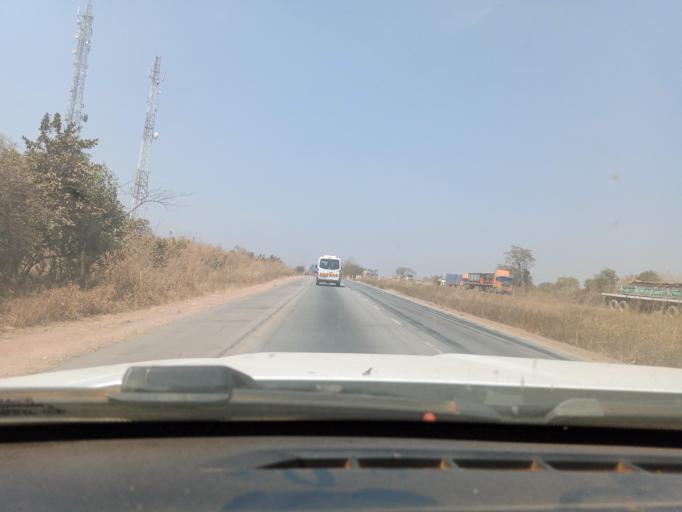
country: ZM
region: Copperbelt
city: Luanshya
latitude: -13.0230
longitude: 28.4428
